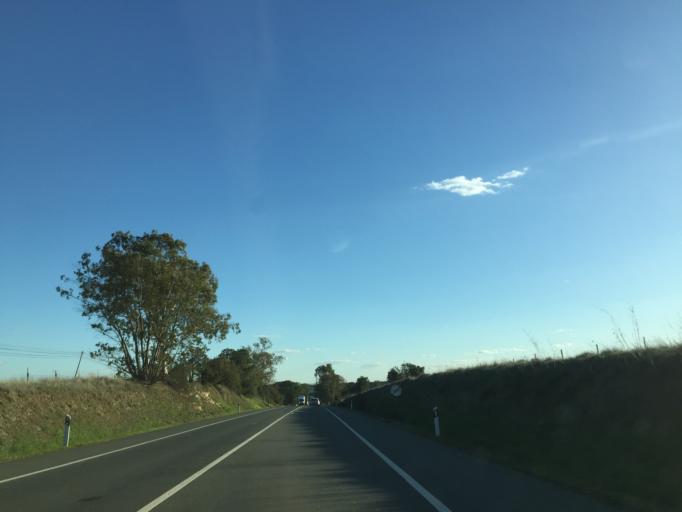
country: PT
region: Setubal
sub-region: Grandola
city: Grandola
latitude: 38.0933
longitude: -8.4184
